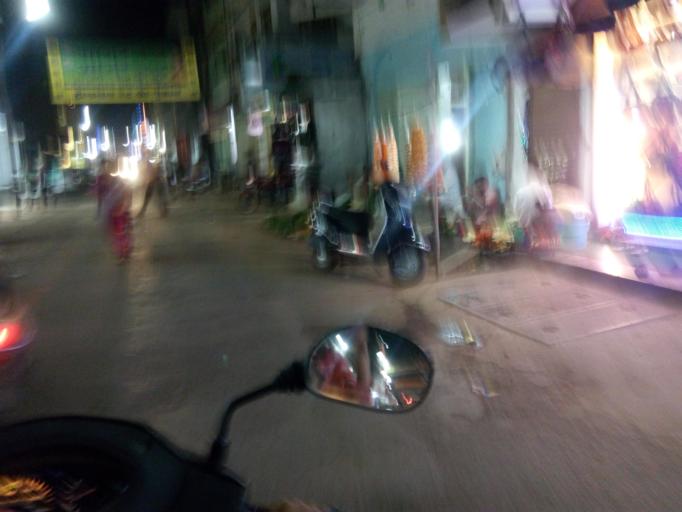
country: IN
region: Maharashtra
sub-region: Gondiya
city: Gondia
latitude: 21.4589
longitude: 80.1925
